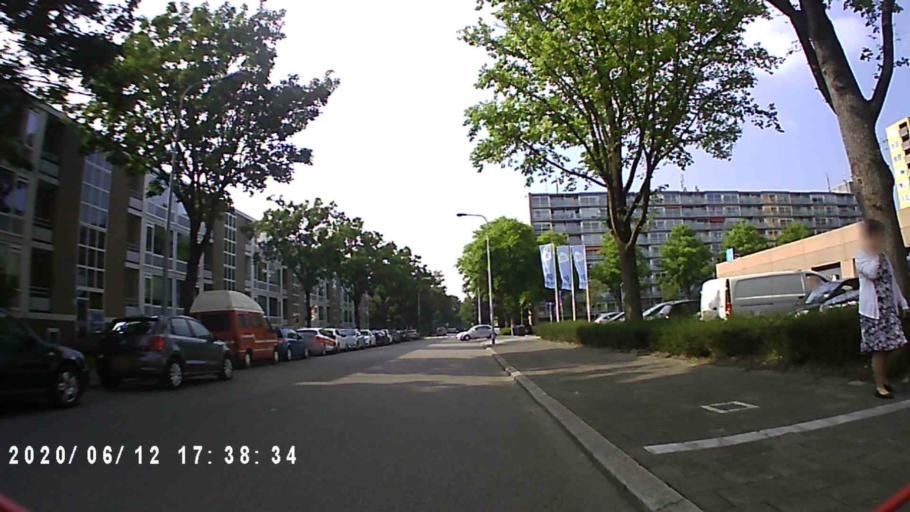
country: NL
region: Groningen
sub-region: Gemeente Groningen
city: Korrewegwijk
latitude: 53.2331
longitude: 6.5524
